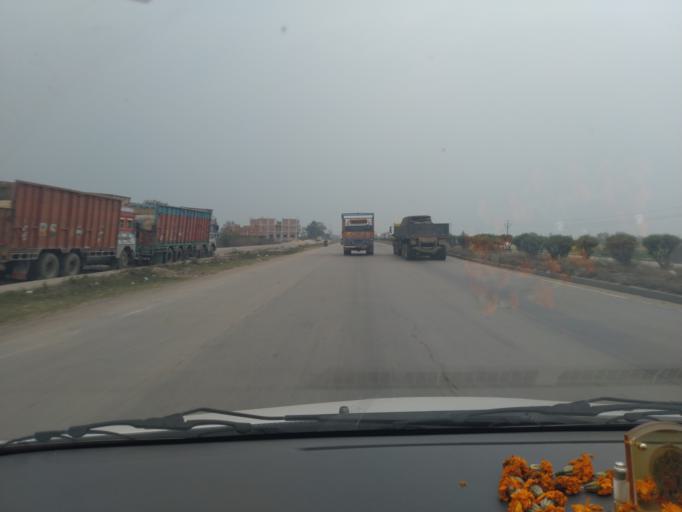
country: IN
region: Bihar
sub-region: Rohtas
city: Dehri
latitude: 24.9739
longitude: 83.9067
